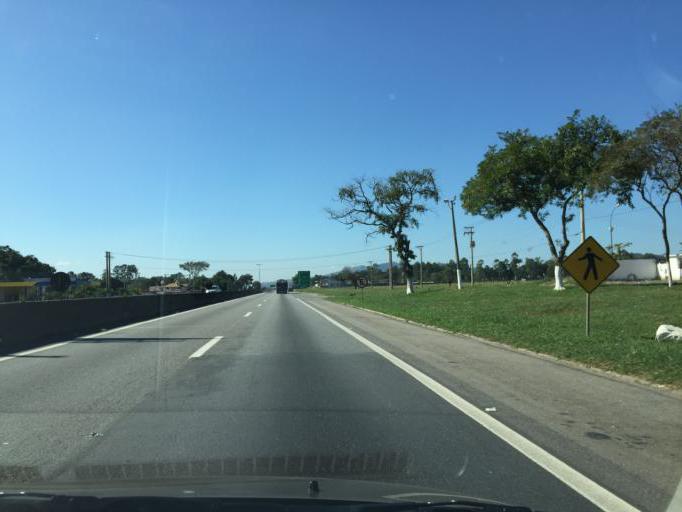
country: BR
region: Sao Paulo
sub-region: Pindamonhangaba
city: Pindamonhangaba
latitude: -22.9285
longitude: -45.3573
